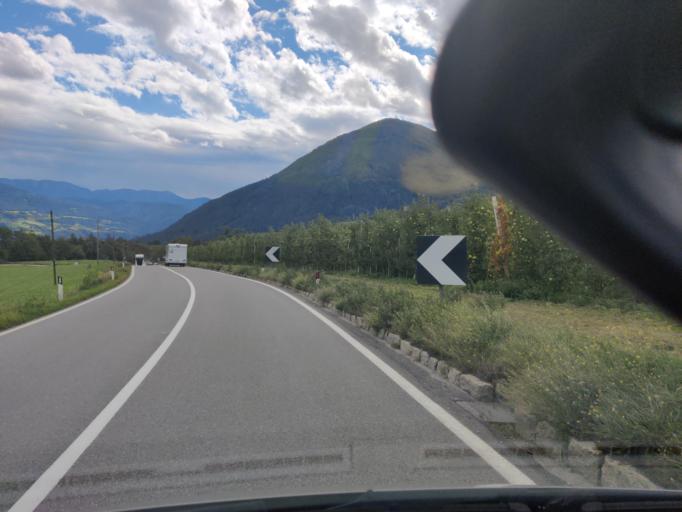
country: IT
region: Trentino-Alto Adige
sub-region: Bolzano
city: Varna
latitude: 46.7547
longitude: 11.6370
